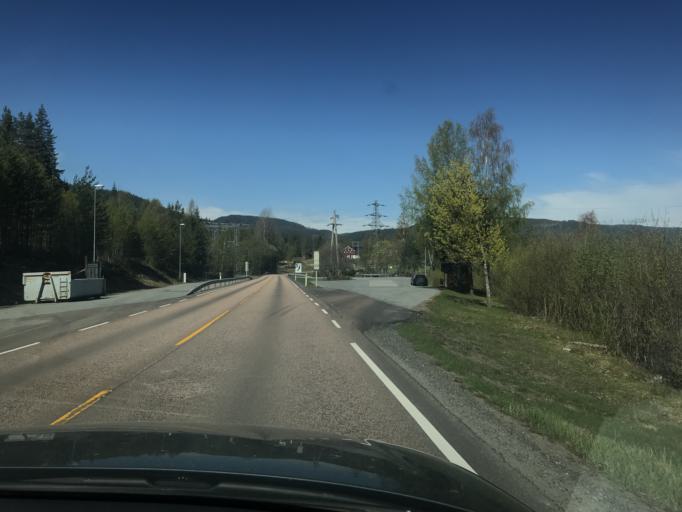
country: NO
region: Buskerud
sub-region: Kongsberg
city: Kongsberg
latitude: 59.7005
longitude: 9.6152
